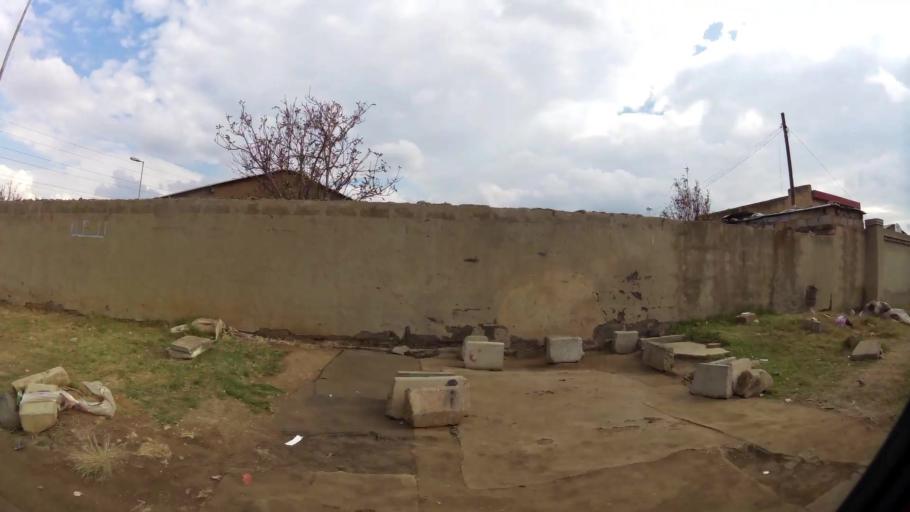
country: ZA
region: Gauteng
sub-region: City of Johannesburg Metropolitan Municipality
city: Soweto
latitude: -26.2386
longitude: 27.8636
